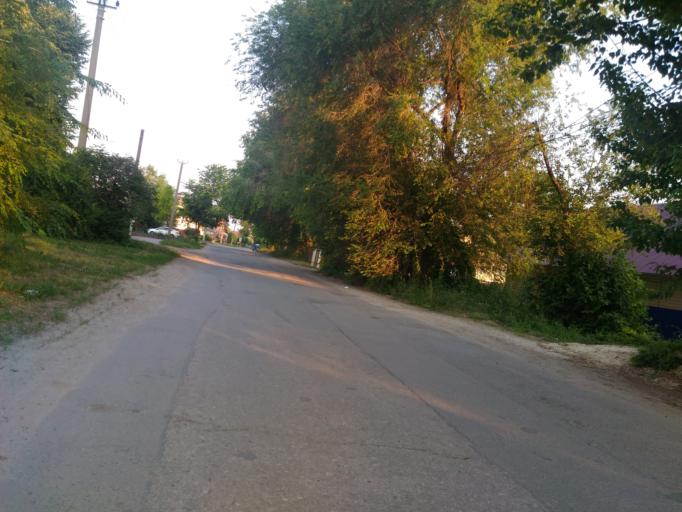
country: RU
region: Ulyanovsk
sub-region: Ulyanovskiy Rayon
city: Ulyanovsk
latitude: 54.3394
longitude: 48.3687
